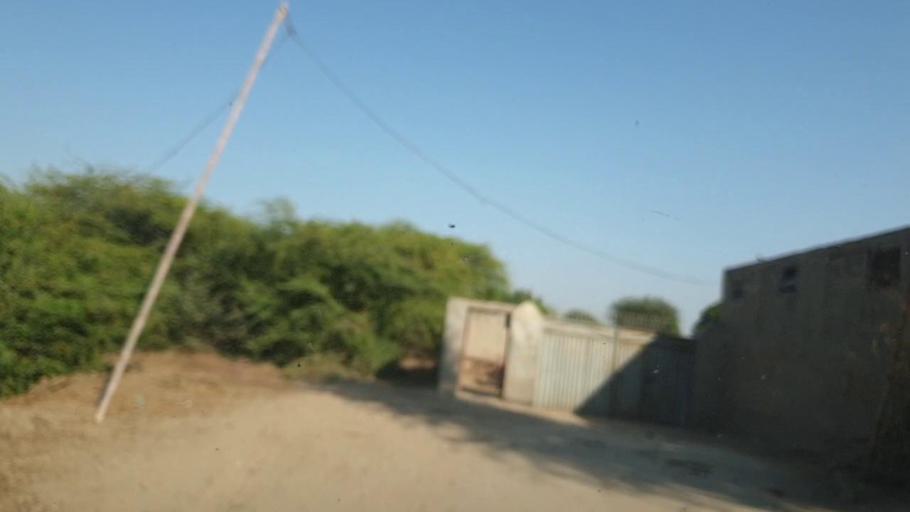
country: PK
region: Sindh
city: Naukot
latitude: 25.0288
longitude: 69.4508
